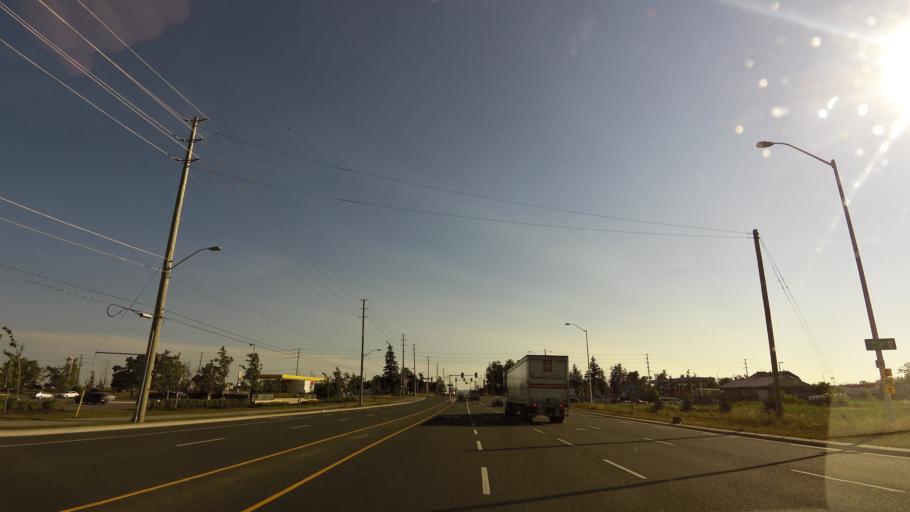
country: CA
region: Ontario
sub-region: Halton
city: Milton
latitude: 43.5762
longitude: -79.8328
